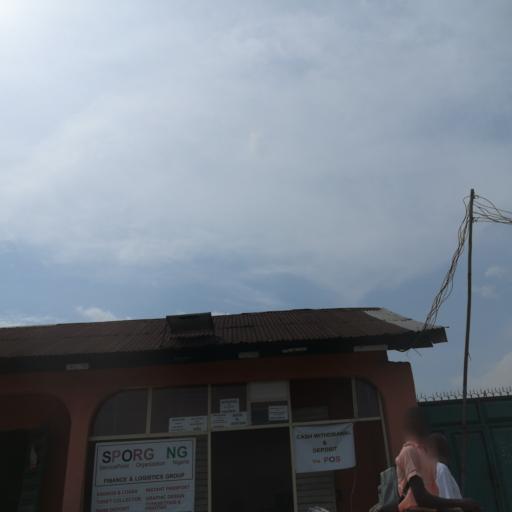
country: NG
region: Rivers
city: Port Harcourt
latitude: 4.8686
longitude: 7.0217
